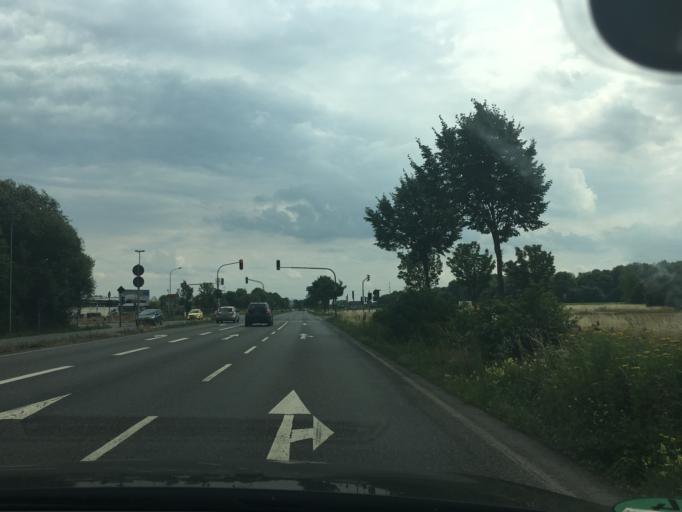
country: DE
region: North Rhine-Westphalia
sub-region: Regierungsbezirk Koln
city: Niederzier
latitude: 50.8498
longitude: 6.4446
